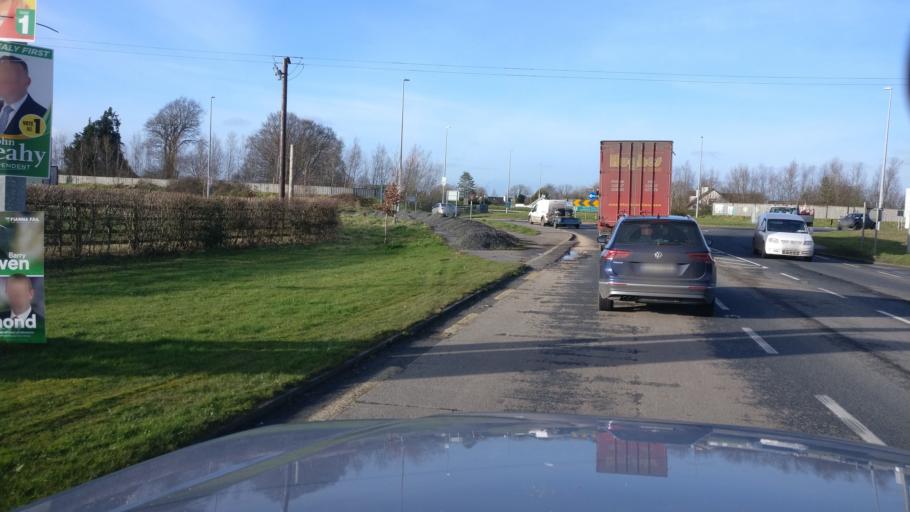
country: IE
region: Leinster
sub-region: Uibh Fhaili
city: Tullamore
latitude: 53.2535
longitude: -7.4778
